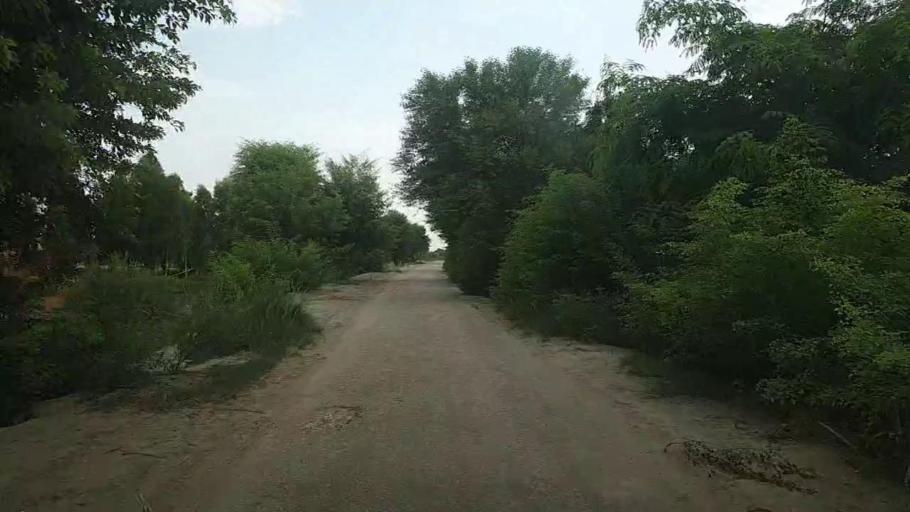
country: PK
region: Sindh
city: Karaundi
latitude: 26.9457
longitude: 68.4102
